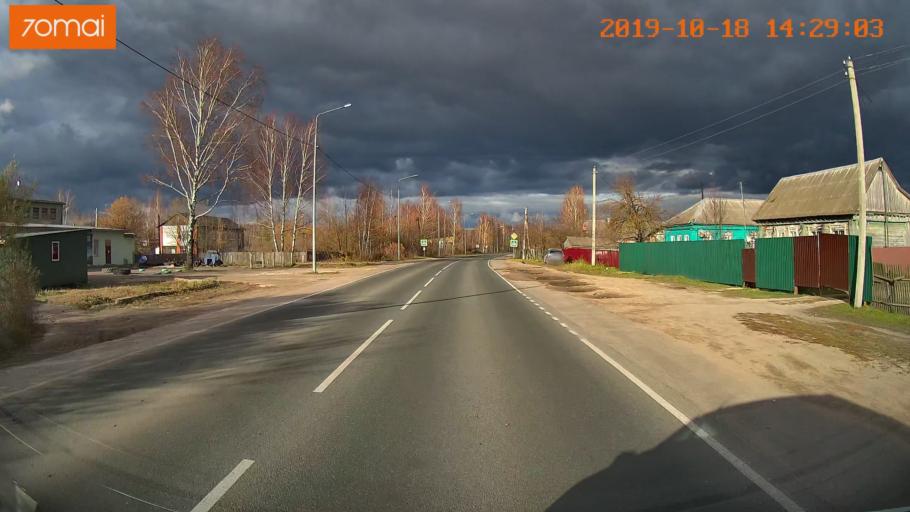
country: RU
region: Rjazan
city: Tuma
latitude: 55.1536
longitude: 40.5553
